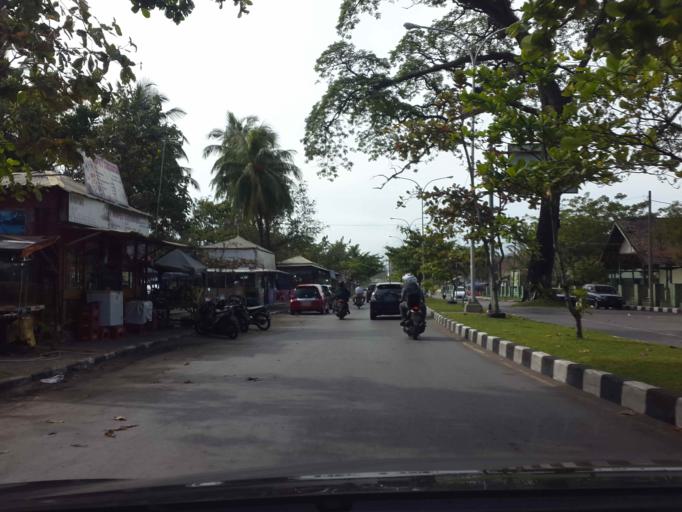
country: ID
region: West Sumatra
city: Padang
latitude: -0.9595
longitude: 100.3533
